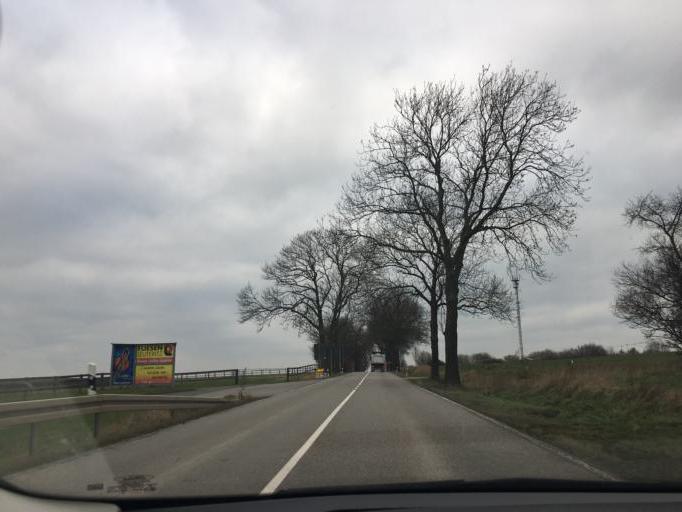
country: DE
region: Saxony
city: Penig
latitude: 50.9431
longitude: 12.6803
